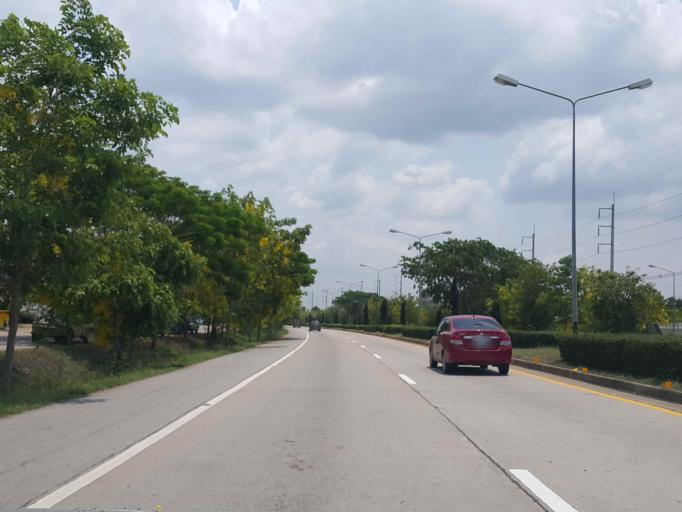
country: TH
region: Lampang
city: Lampang
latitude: 18.2772
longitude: 99.4548
